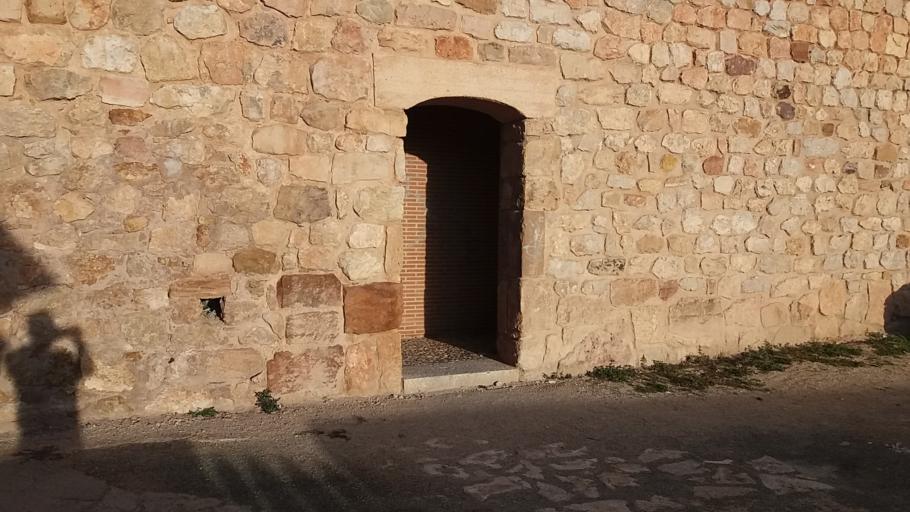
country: ES
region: Castille-La Mancha
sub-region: Provincia de Guadalajara
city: Atienza
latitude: 41.1985
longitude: -2.8703
